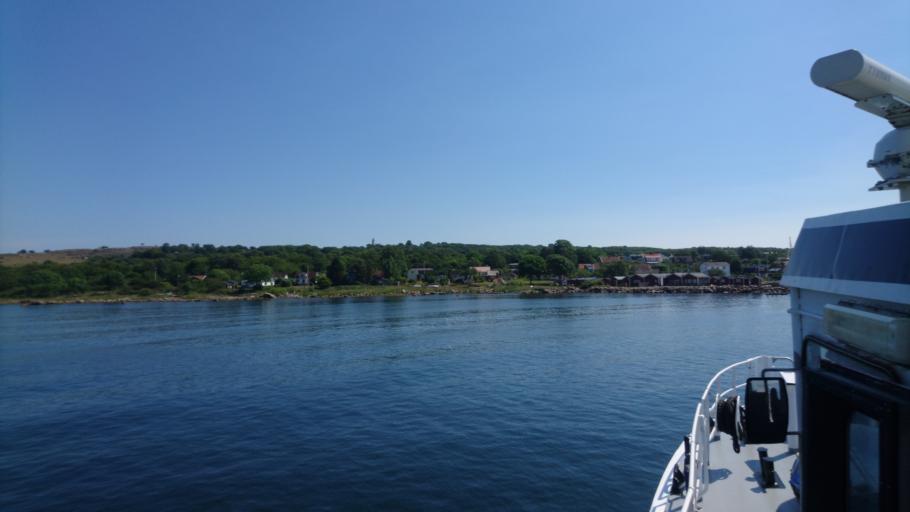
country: SE
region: Blekinge
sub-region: Karlshamns Kommun
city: Karlshamn
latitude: 56.0109
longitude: 14.8324
